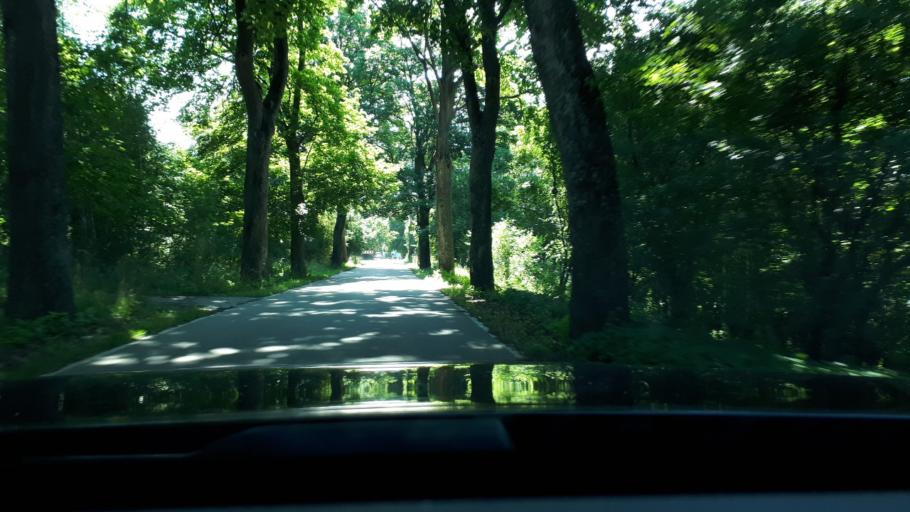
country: PL
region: Warmian-Masurian Voivodeship
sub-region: Powiat ostrodzki
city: Ostroda
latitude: 53.6845
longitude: 20.0605
